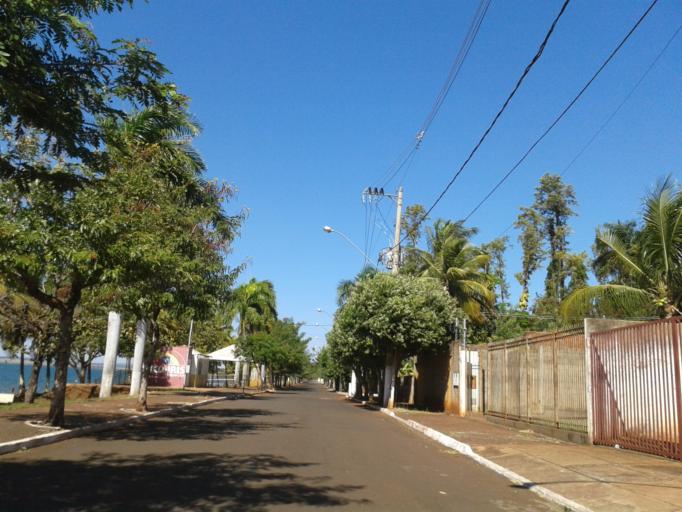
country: BR
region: Minas Gerais
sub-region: Capinopolis
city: Capinopolis
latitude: -18.5185
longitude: -49.4979
